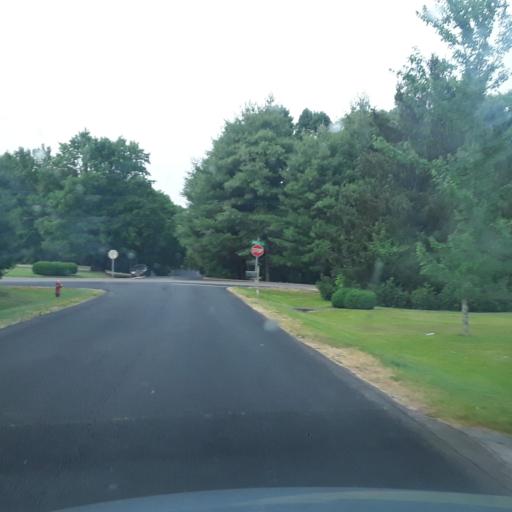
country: US
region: Tennessee
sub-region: Williamson County
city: Brentwood
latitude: 36.0599
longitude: -86.7639
